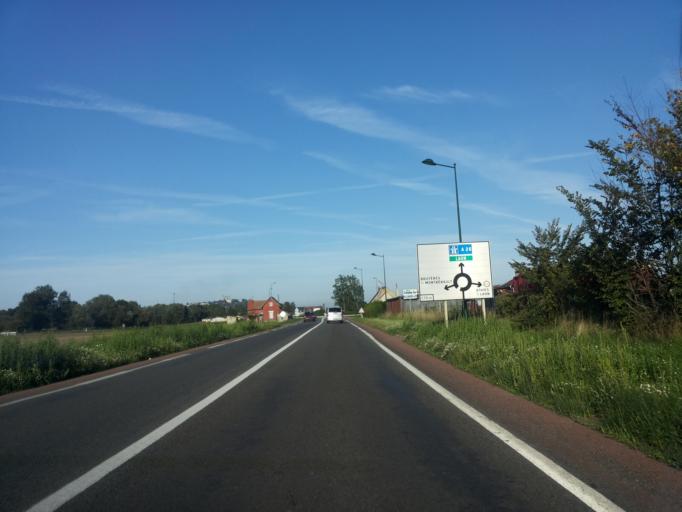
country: FR
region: Picardie
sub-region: Departement de l'Aisne
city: Athies-sous-Laon
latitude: 49.5626
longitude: 3.6895
